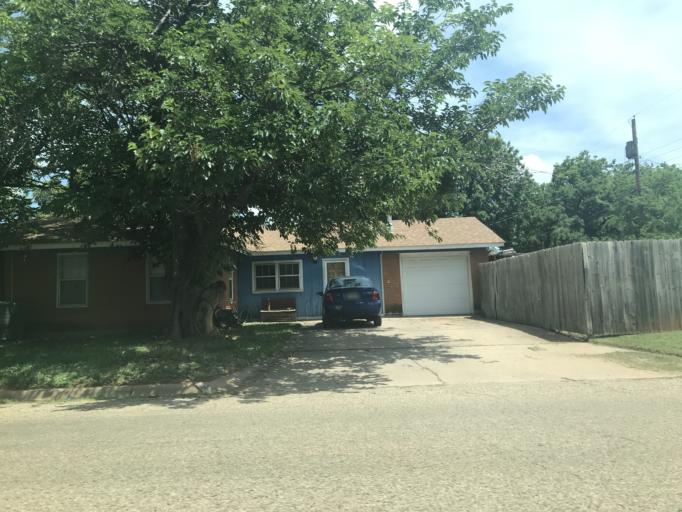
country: US
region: Texas
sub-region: Taylor County
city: Abilene
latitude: 32.4654
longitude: -99.7618
